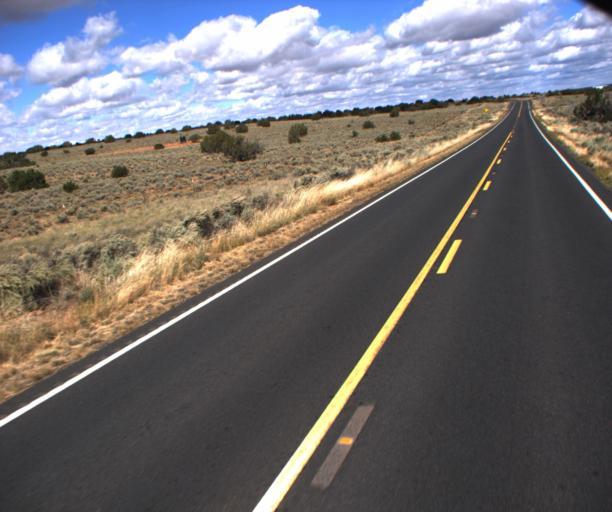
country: US
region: Arizona
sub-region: Apache County
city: Houck
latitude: 35.1631
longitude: -109.3371
